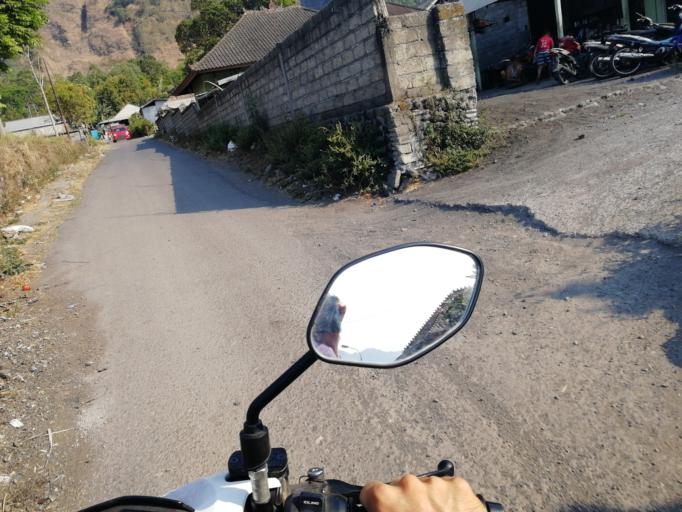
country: ID
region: Bali
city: Banjar Trunyan
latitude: -8.2736
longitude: 115.4135
